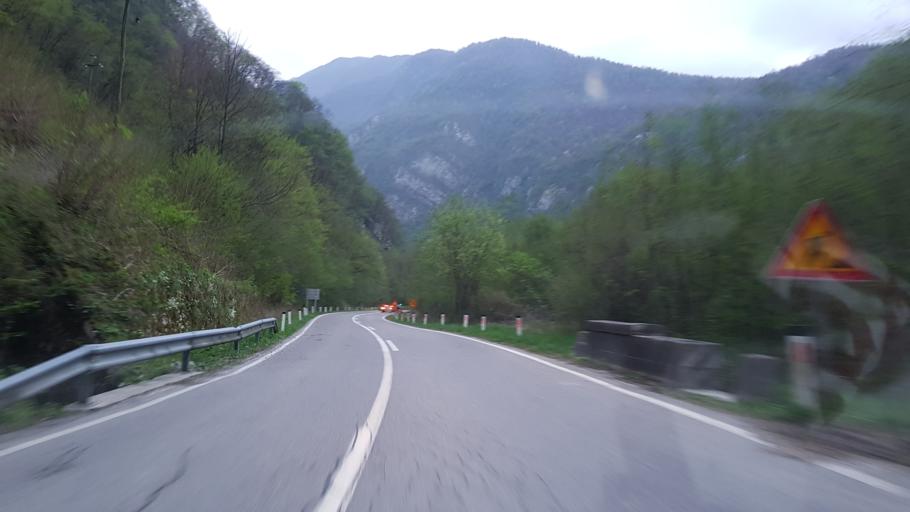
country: SI
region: Kobarid
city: Kobarid
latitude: 46.2427
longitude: 13.5090
